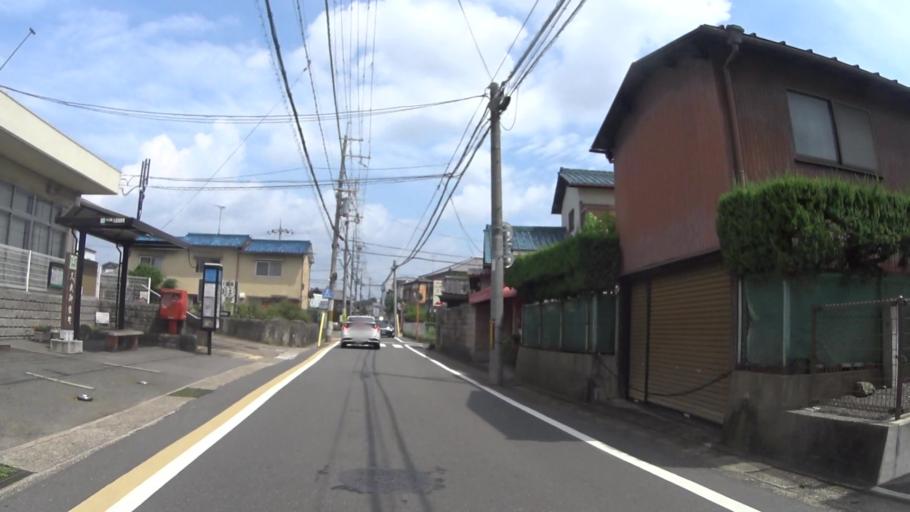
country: JP
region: Kyoto
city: Muko
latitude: 34.9419
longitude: 135.7330
